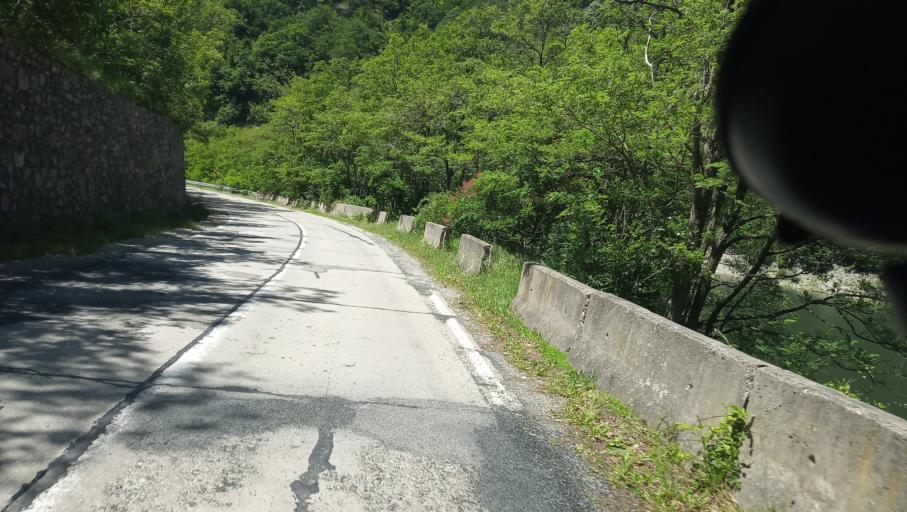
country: RO
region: Caras-Severin
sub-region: Comuna Mehadia
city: Valea Bolvasnita
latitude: 44.9518
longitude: 22.4736
